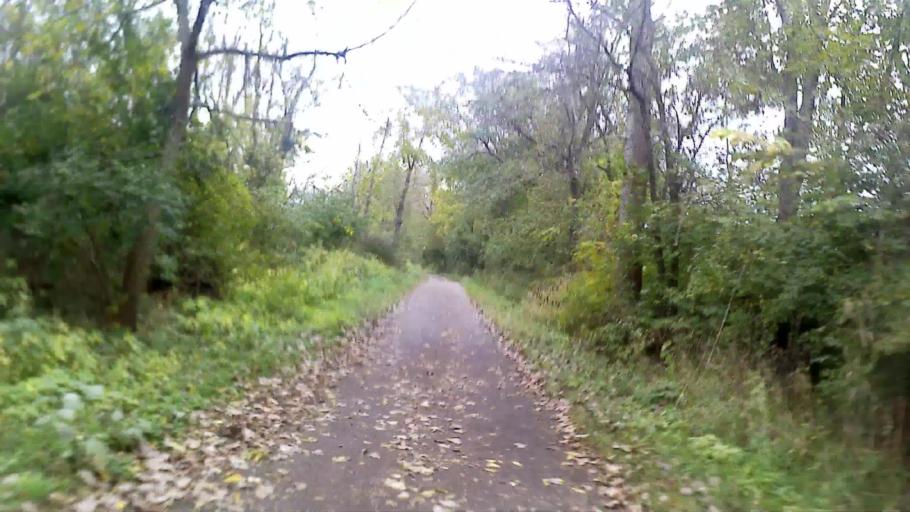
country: US
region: Illinois
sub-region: Kane County
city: Sugar Grove
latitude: 41.7770
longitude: -88.4249
